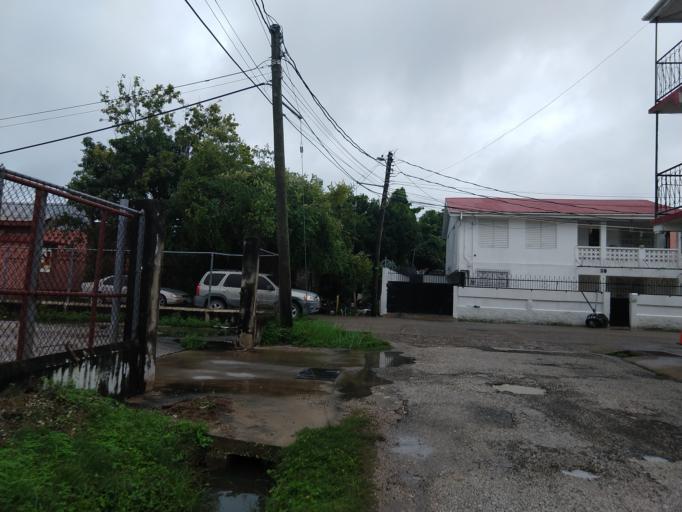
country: BZ
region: Belize
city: Belize City
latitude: 17.5028
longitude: -88.1913
